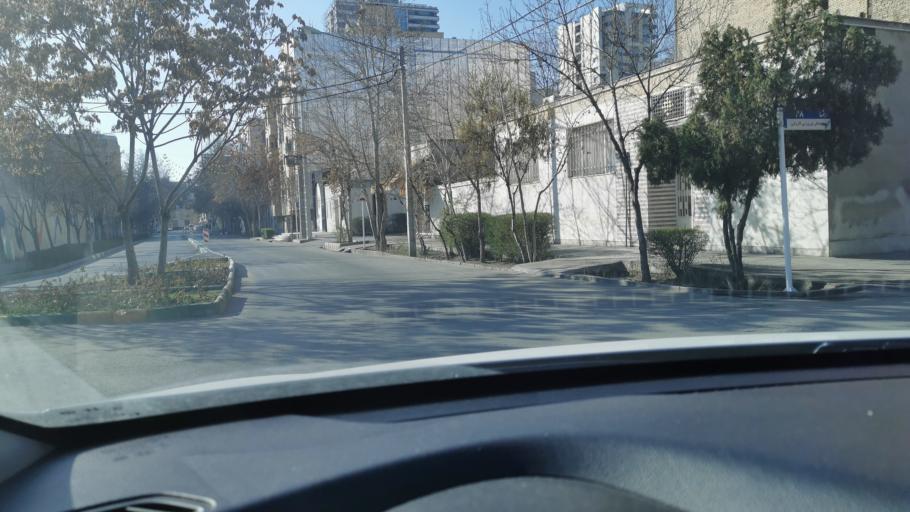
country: IR
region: Razavi Khorasan
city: Mashhad
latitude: 36.2863
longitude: 59.5672
